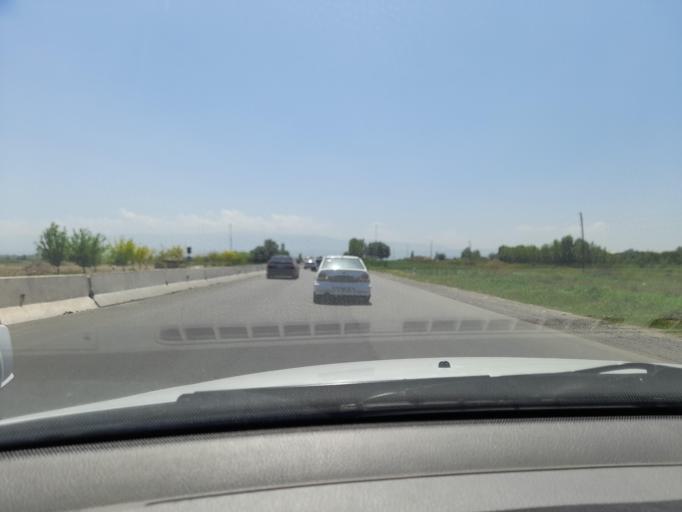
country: UZ
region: Jizzax
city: Jizzax
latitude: 40.1461
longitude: 67.9558
